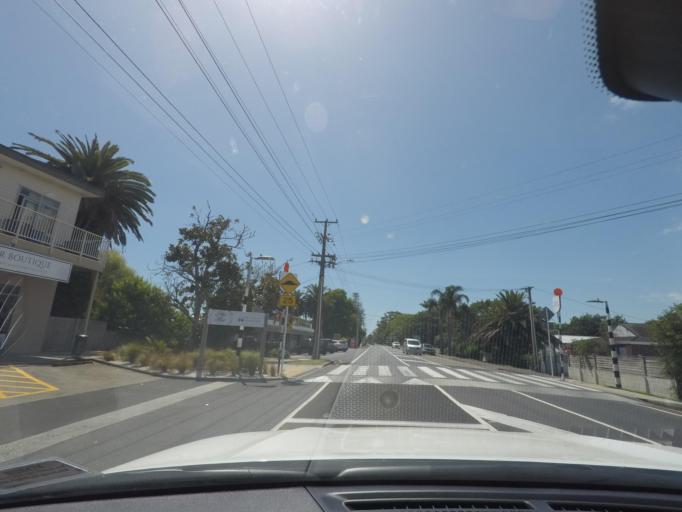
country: NZ
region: Auckland
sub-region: Auckland
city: Parakai
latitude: -36.6617
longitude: 174.4342
